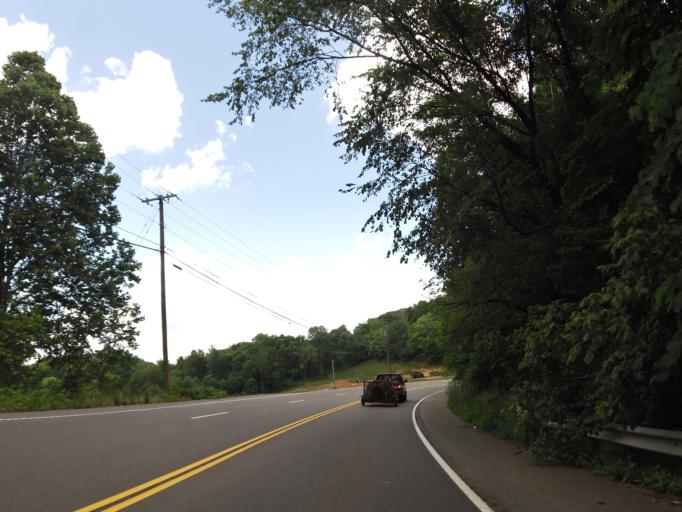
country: US
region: Tennessee
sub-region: Union County
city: Maynardville
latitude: 36.2949
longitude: -83.7605
